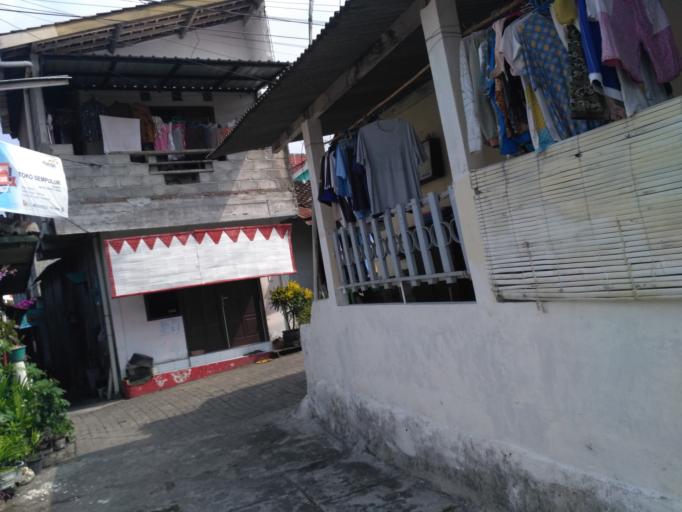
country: ID
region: Daerah Istimewa Yogyakarta
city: Yogyakarta
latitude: -7.7601
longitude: 110.3712
